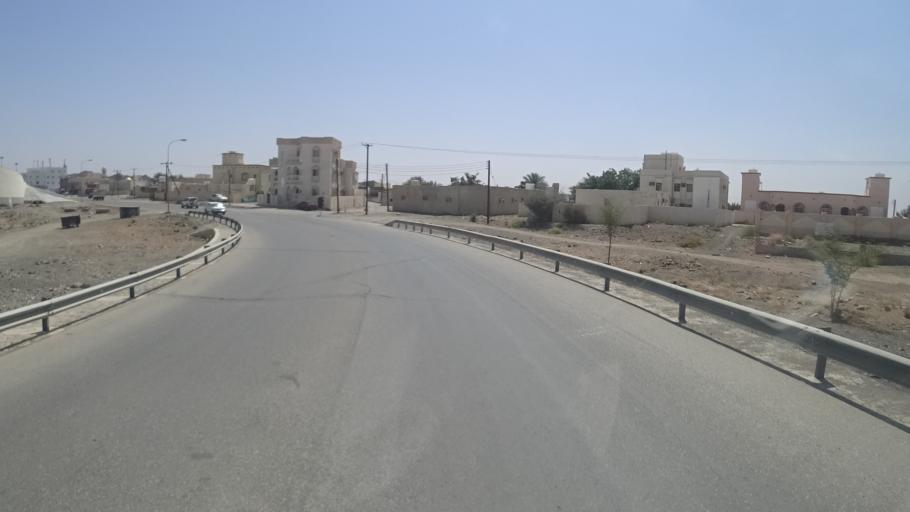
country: OM
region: Ash Sharqiyah
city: Ibra'
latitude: 22.6880
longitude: 58.5421
